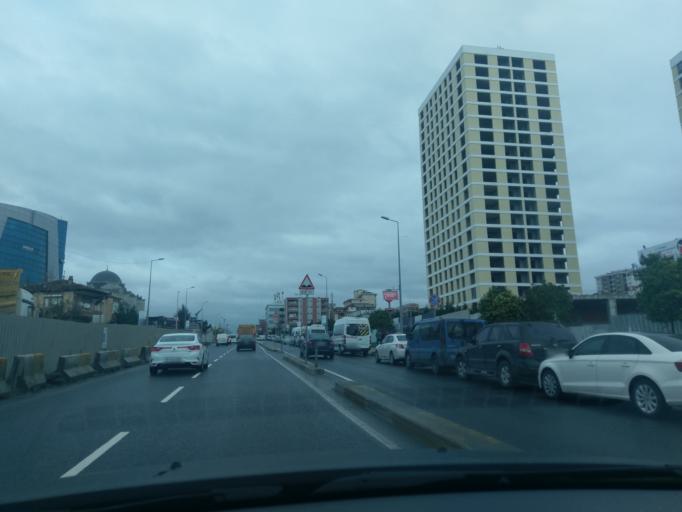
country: TR
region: Istanbul
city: Mahmutbey
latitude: 41.0549
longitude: 28.8305
